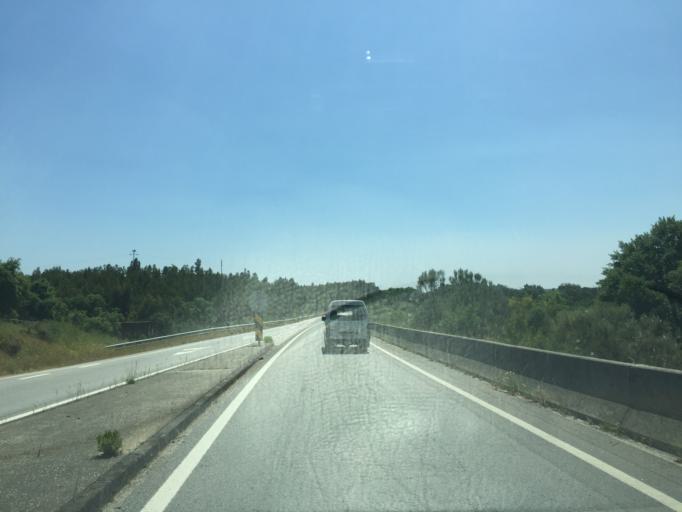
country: PT
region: Santarem
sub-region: Abrantes
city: Alferrarede
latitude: 39.5191
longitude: -8.1601
